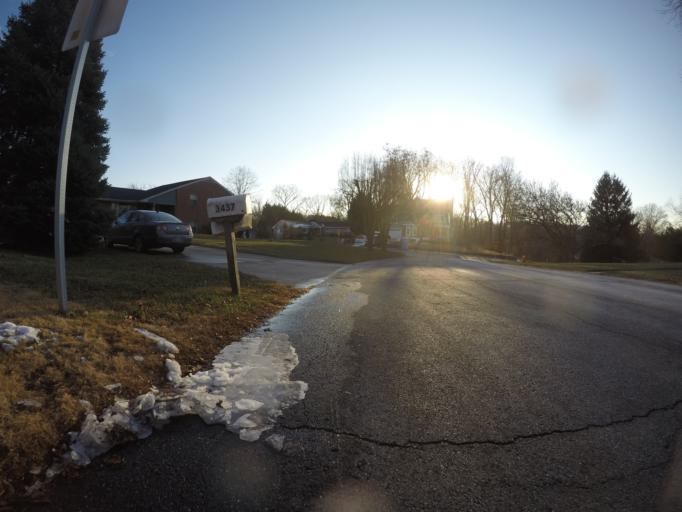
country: US
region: Maryland
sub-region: Howard County
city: Columbia
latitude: 39.2735
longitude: -76.8549
